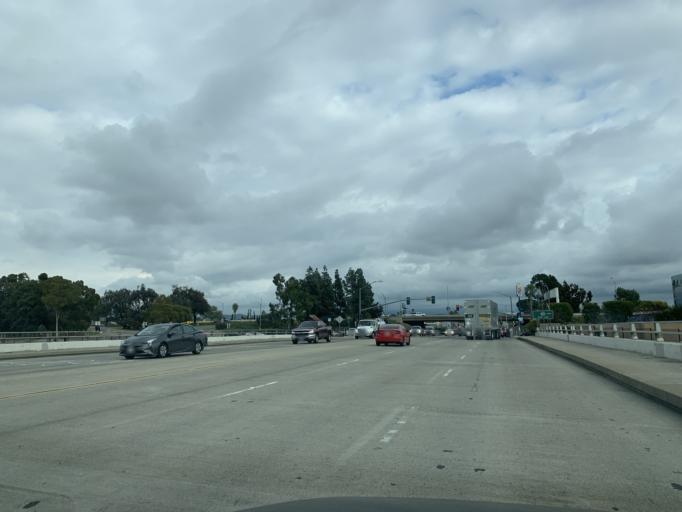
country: US
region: California
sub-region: Orange County
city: Orange
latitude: 33.7878
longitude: -117.8824
